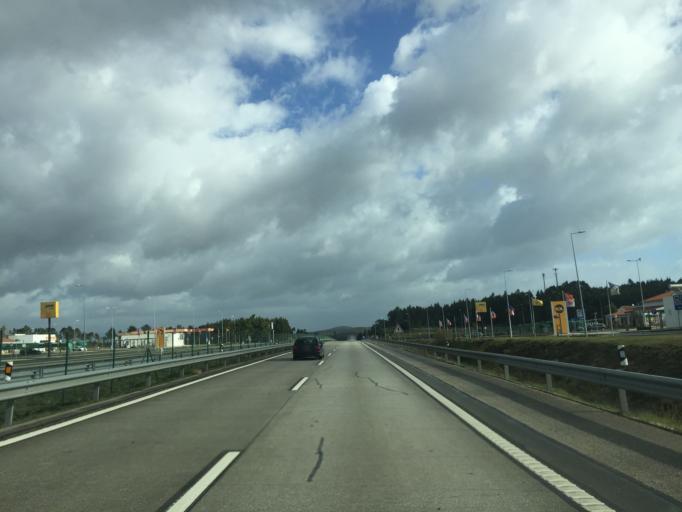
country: PT
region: Lisbon
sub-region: Torres Vedras
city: A dos Cunhados
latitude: 39.1563
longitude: -9.2285
